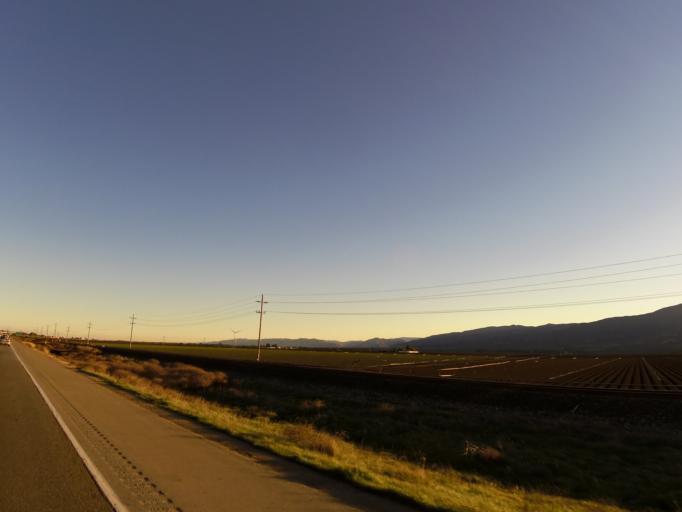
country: US
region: California
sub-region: Monterey County
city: Soledad
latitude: 36.4427
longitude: -121.3543
